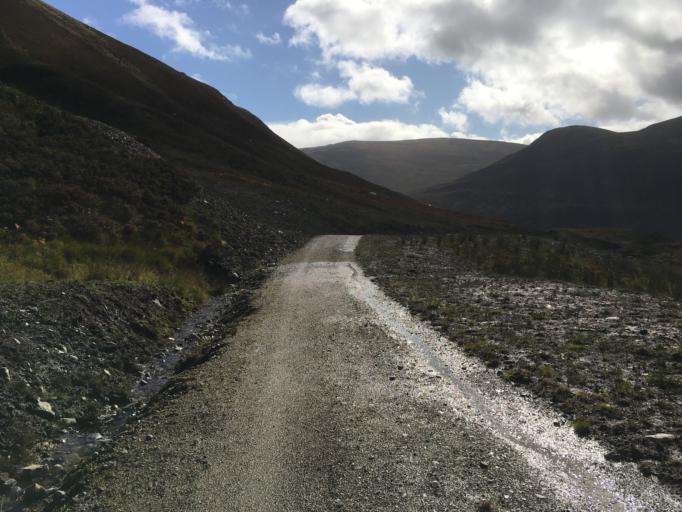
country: GB
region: Scotland
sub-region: Highland
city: Spean Bridge
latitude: 57.3501
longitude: -4.9833
